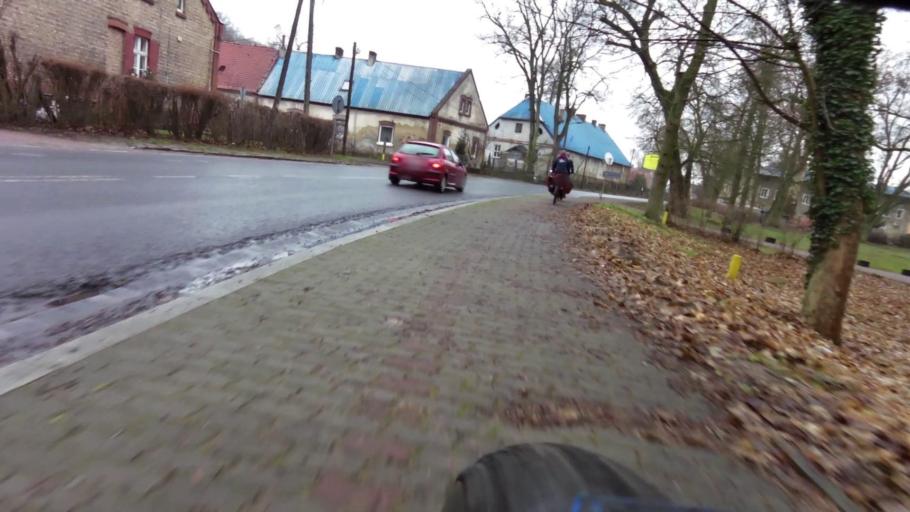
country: PL
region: Lubusz
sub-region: Powiat gorzowski
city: Kostrzyn nad Odra
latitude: 52.6203
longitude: 14.7047
